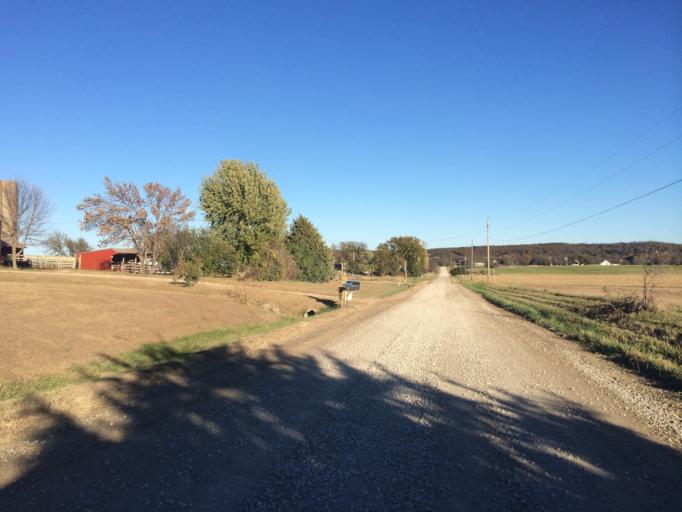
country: US
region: Kansas
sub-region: Douglas County
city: Lawrence
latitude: 38.8916
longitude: -95.3273
